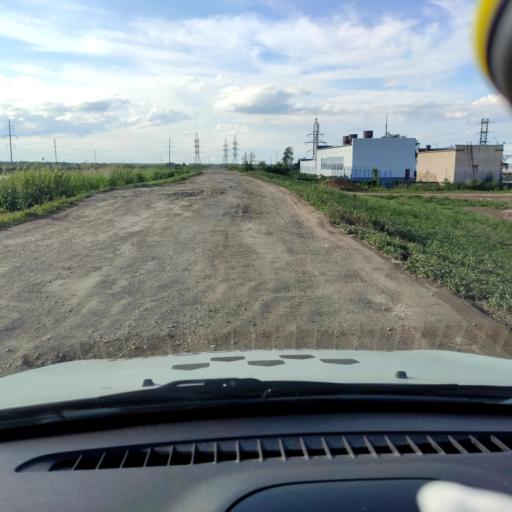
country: RU
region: Samara
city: Tol'yatti
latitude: 53.5912
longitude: 49.4394
